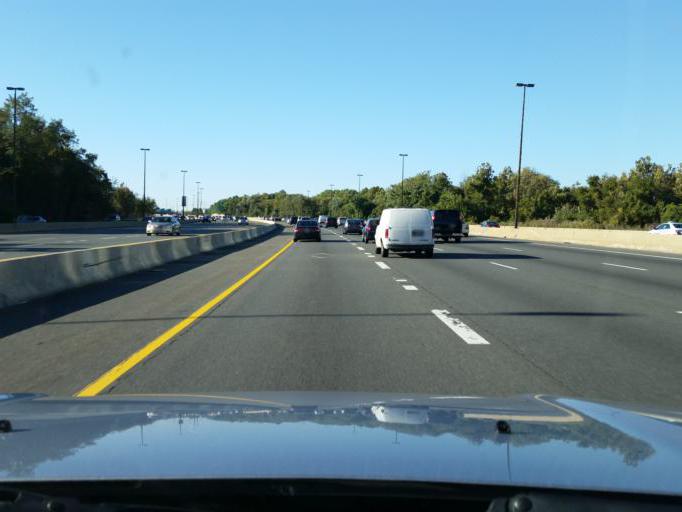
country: US
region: Maryland
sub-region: Montgomery County
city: Rockville
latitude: 39.0673
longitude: -77.1578
